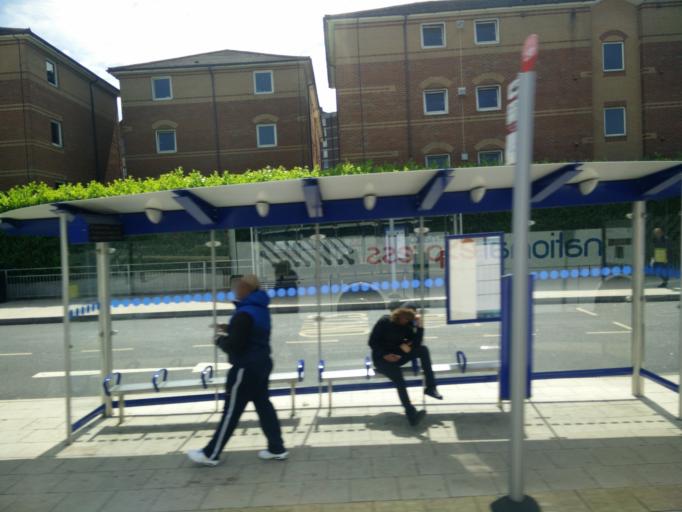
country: GB
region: England
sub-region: Luton
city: Luton
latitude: 51.8822
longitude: -0.4157
